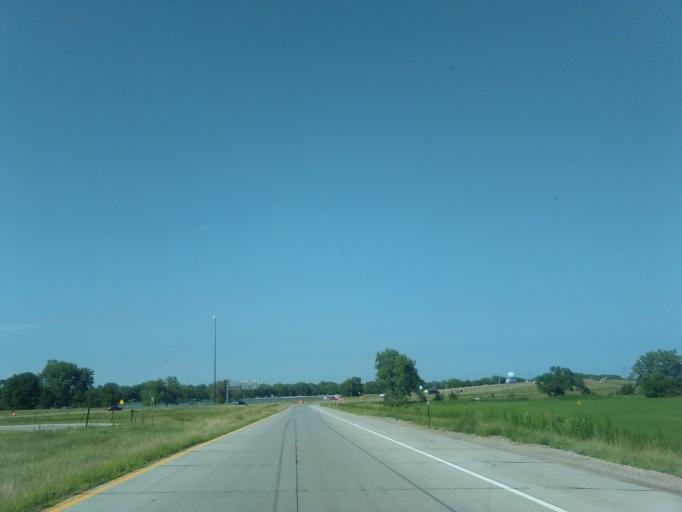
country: US
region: Nebraska
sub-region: Hall County
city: Grand Island
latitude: 40.8188
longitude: -98.3771
